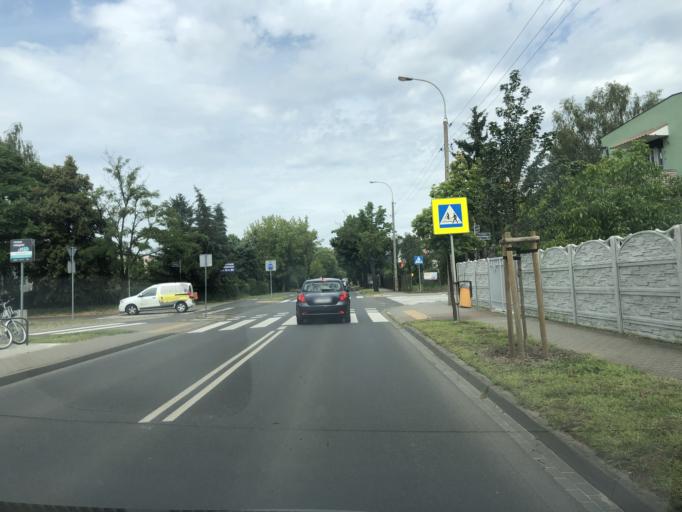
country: PL
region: Greater Poland Voivodeship
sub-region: Powiat poznanski
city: Lubon
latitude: 52.3599
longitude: 16.8809
